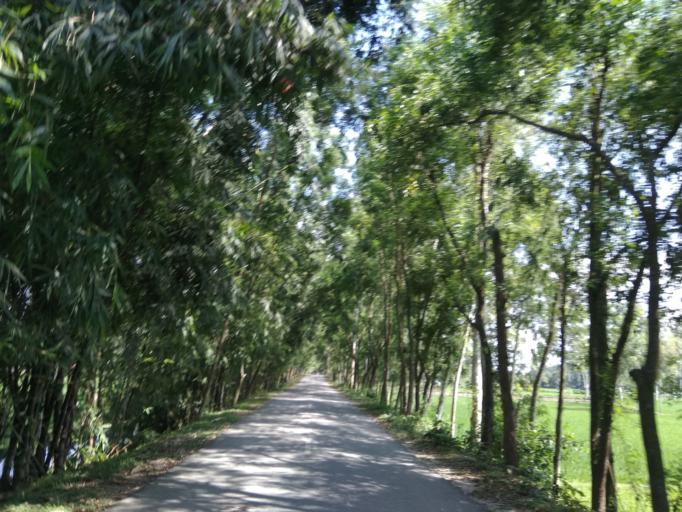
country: IN
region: West Bengal
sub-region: Koch Bihar
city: Haldibari
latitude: 26.1939
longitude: 88.6903
